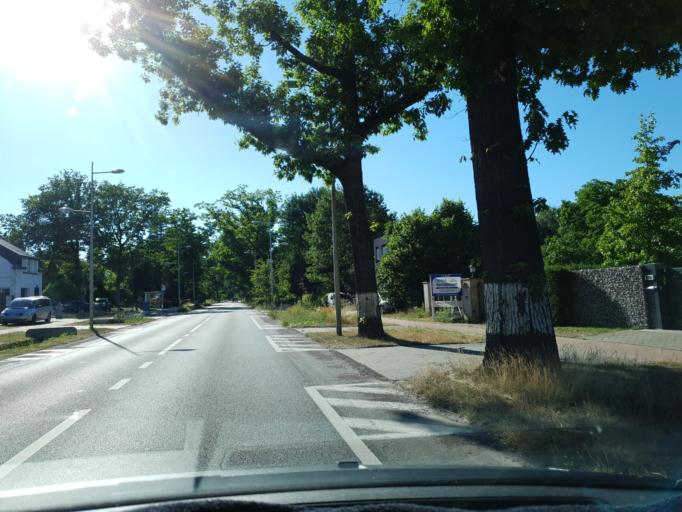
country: BE
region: Flanders
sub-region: Provincie Antwerpen
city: Nijlen
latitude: 51.1641
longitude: 4.7012
